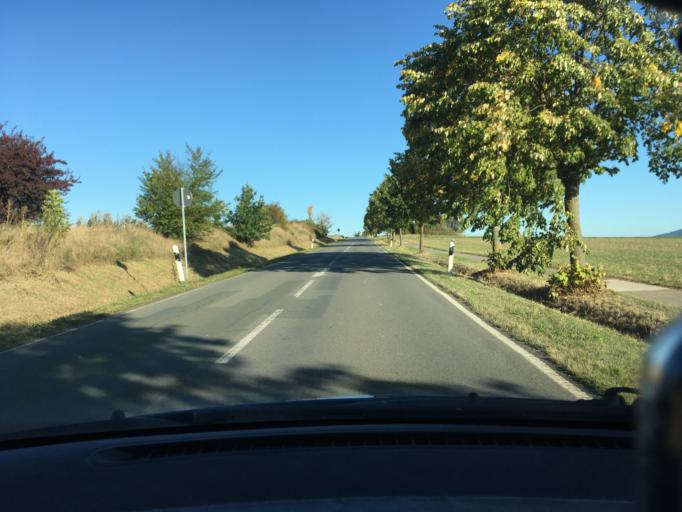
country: DE
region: Lower Saxony
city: Hulsede
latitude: 52.2123
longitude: 9.3916
